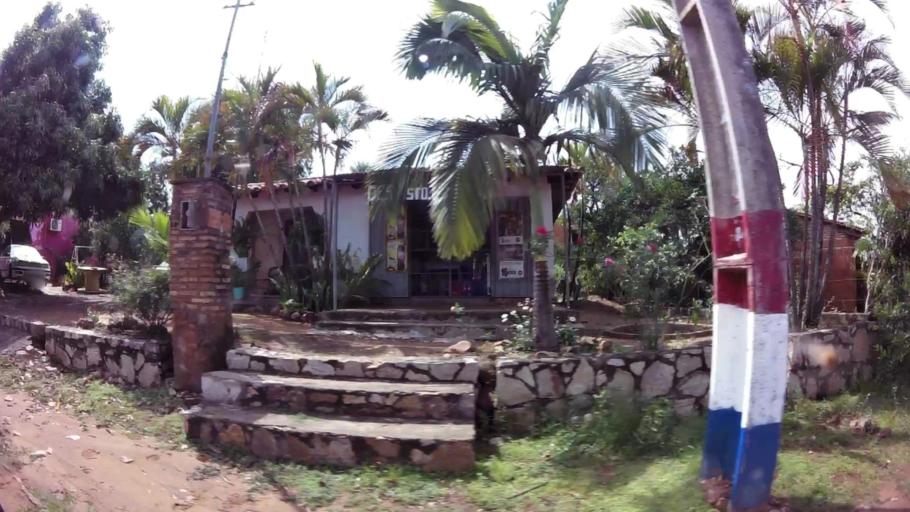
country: PY
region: Central
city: Limpio
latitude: -25.1740
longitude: -57.4423
